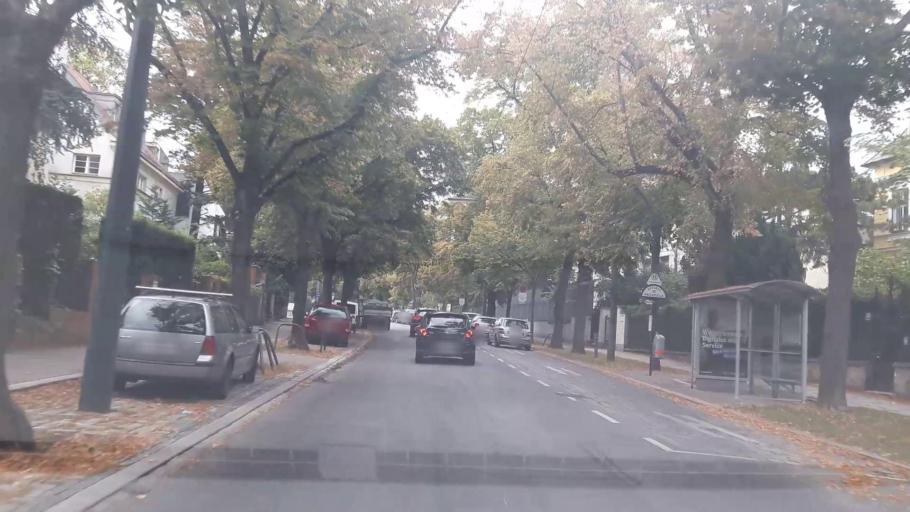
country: AT
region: Lower Austria
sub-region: Politischer Bezirk Korneuburg
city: Langenzersdorf
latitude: 48.2544
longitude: 16.3494
